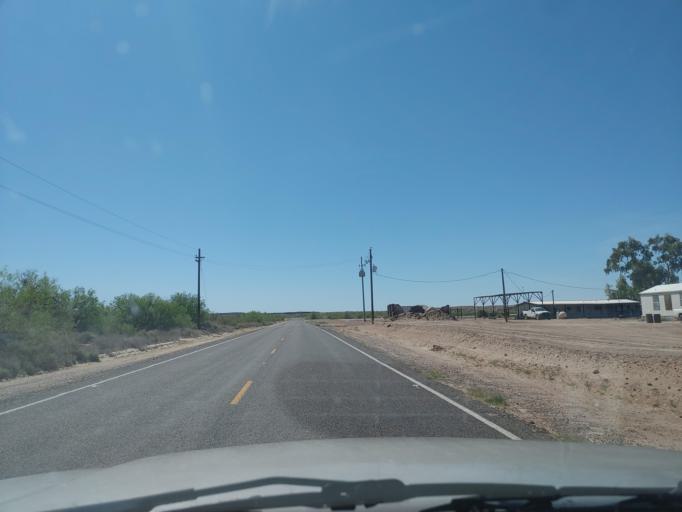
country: US
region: Arizona
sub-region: Maricopa County
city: Gila Bend
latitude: 32.9489
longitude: -113.3060
